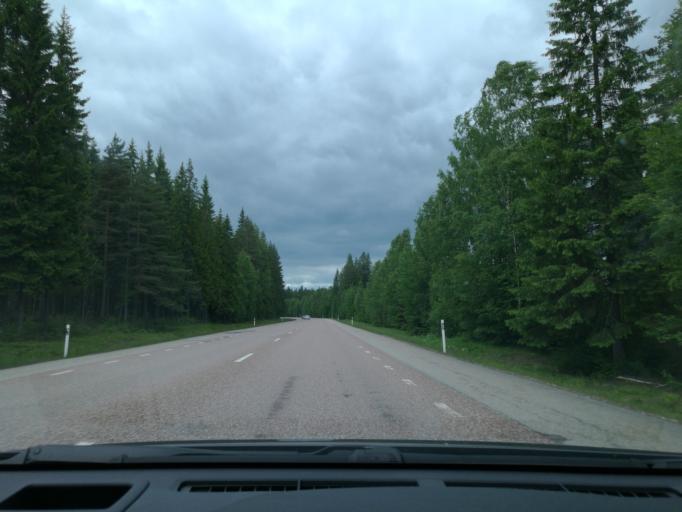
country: SE
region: Dalarna
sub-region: Smedjebackens Kommun
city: Smedjebacken
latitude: 60.1056
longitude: 15.4964
